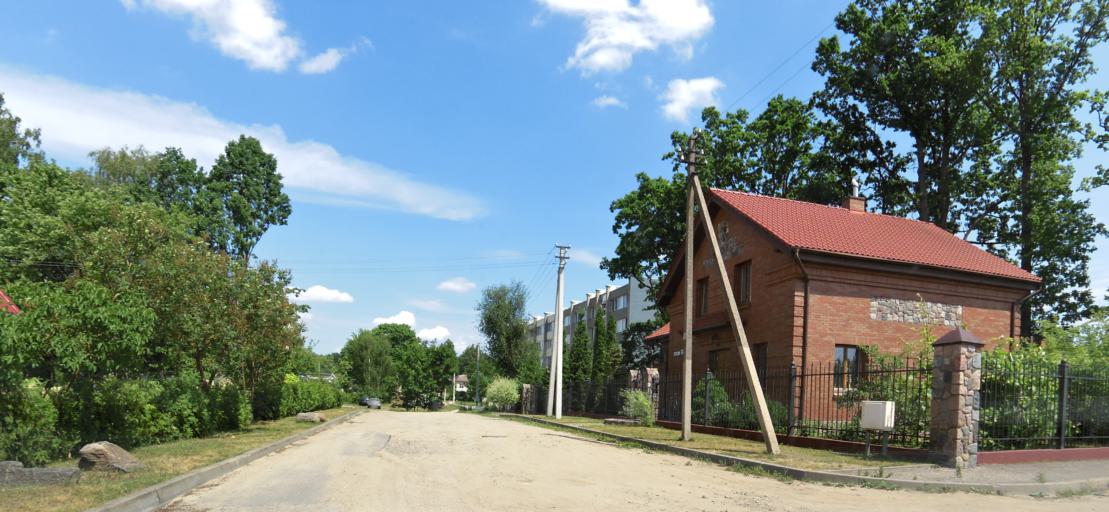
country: LT
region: Vilnius County
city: Pasilaiciai
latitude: 54.7609
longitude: 25.2064
